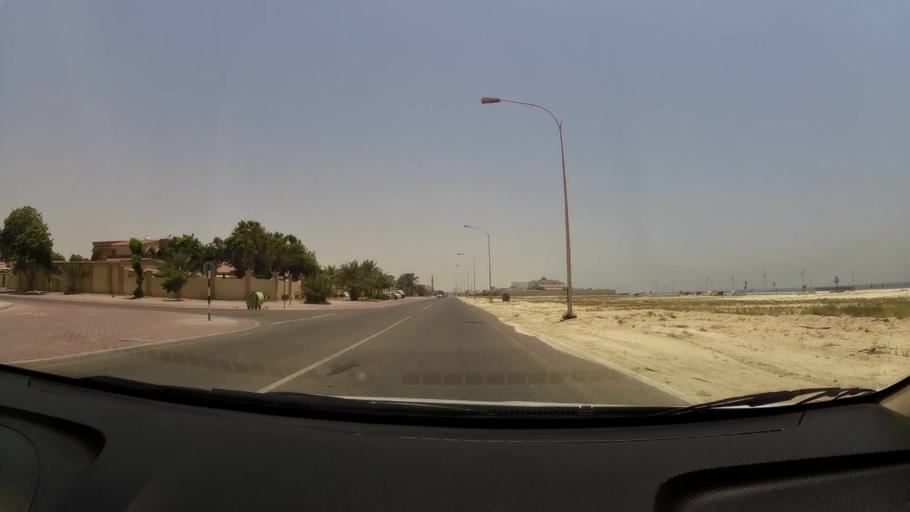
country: AE
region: Umm al Qaywayn
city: Umm al Qaywayn
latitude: 25.5432
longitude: 55.5366
